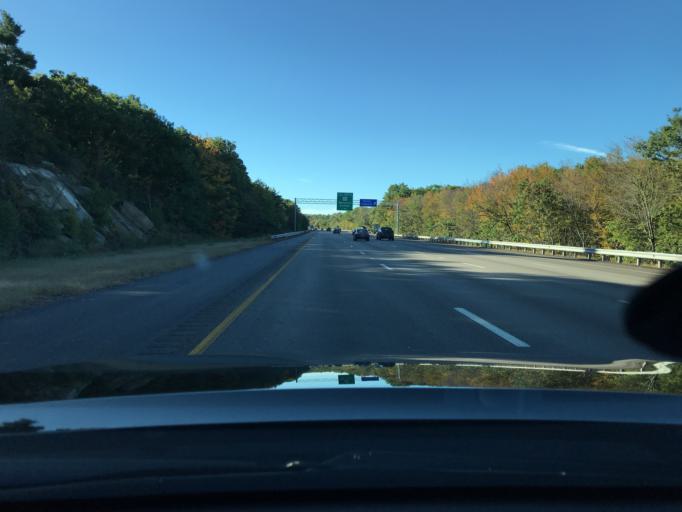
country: US
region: Massachusetts
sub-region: Norfolk County
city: Needham
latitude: 42.2592
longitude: -71.2103
